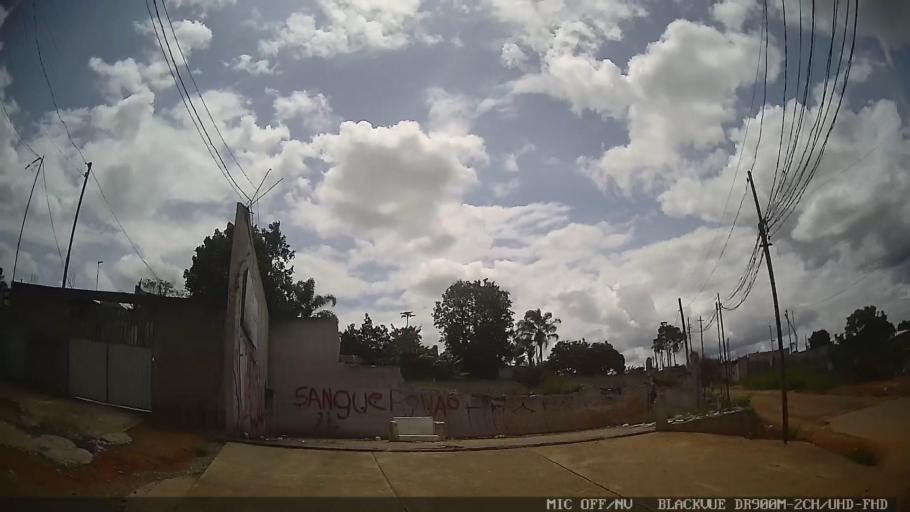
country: BR
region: Sao Paulo
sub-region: Mogi das Cruzes
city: Mogi das Cruzes
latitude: -23.5929
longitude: -46.2344
